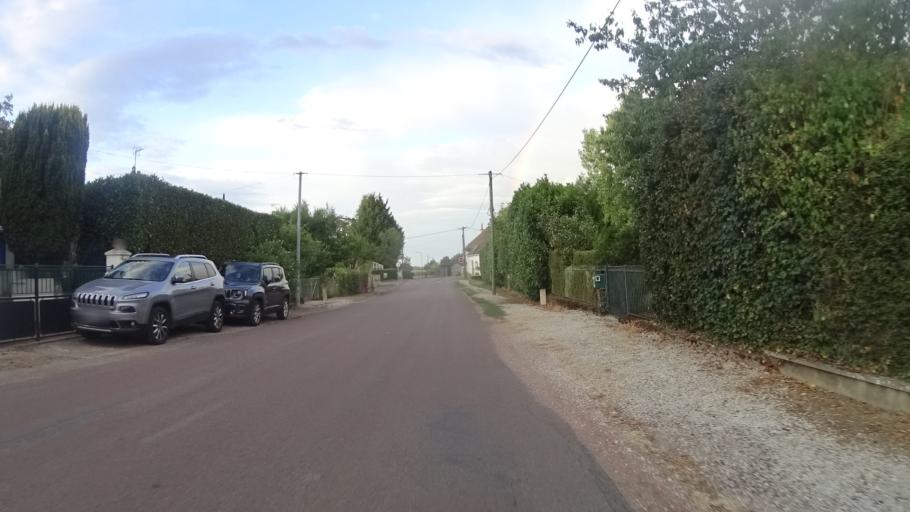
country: FR
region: Bourgogne
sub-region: Departement de la Cote-d'Or
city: Seurre
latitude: 46.9746
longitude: 5.0925
